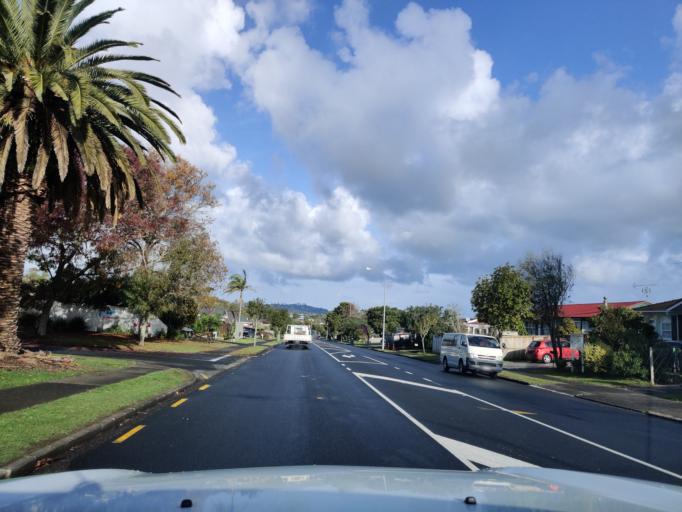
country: NZ
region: Auckland
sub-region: Auckland
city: Pakuranga
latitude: -36.9067
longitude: 174.8966
